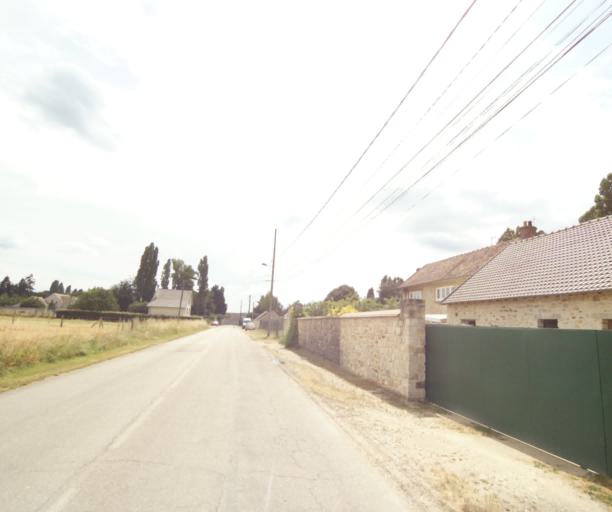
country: FR
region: Ile-de-France
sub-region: Departement de Seine-et-Marne
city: Barbizon
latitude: 48.4333
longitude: 2.5877
